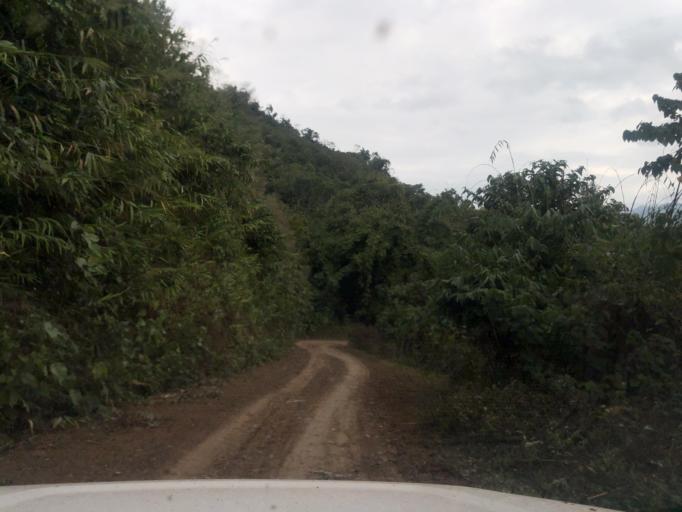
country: LA
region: Phongsali
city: Khoa
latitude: 21.2925
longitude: 102.5847
